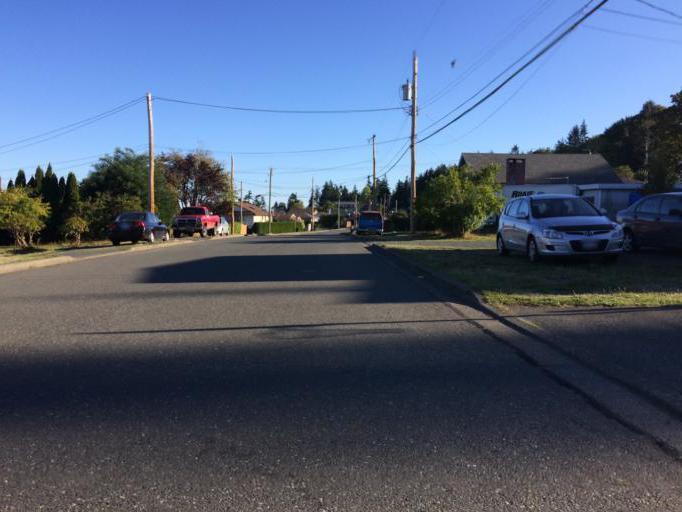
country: CA
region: British Columbia
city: Campbell River
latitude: 50.0202
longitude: -125.2395
